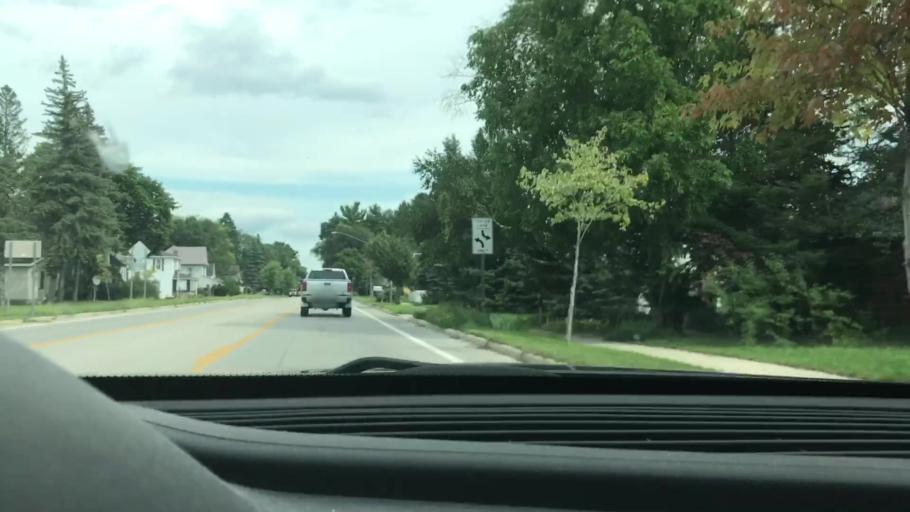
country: US
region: Michigan
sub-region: Antrim County
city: Bellaire
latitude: 44.9754
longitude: -85.2048
